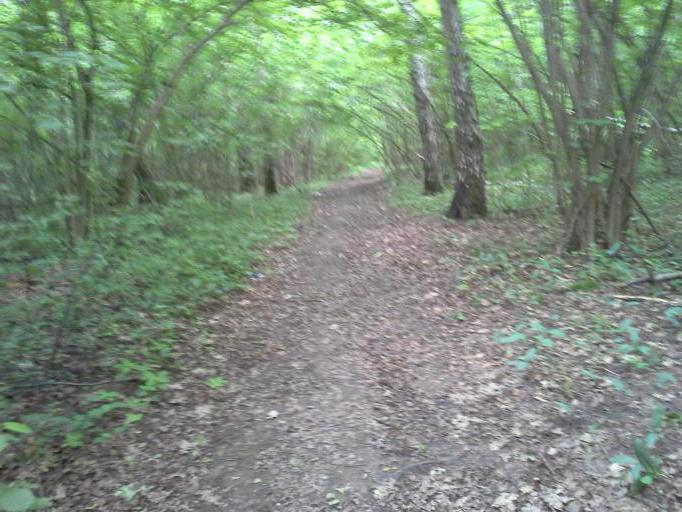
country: RU
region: Moskovskaya
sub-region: Leninskiy Rayon
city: Vnukovo
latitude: 55.6402
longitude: 37.2852
